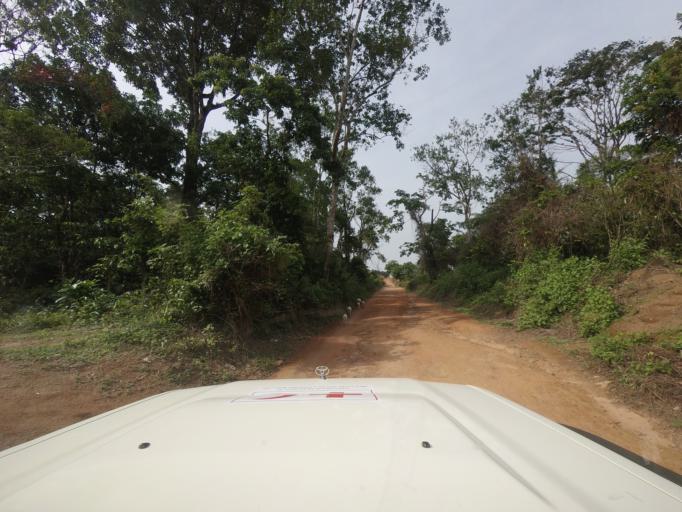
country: GN
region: Nzerekore
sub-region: Macenta
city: Macenta
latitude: 8.5268
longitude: -9.5072
